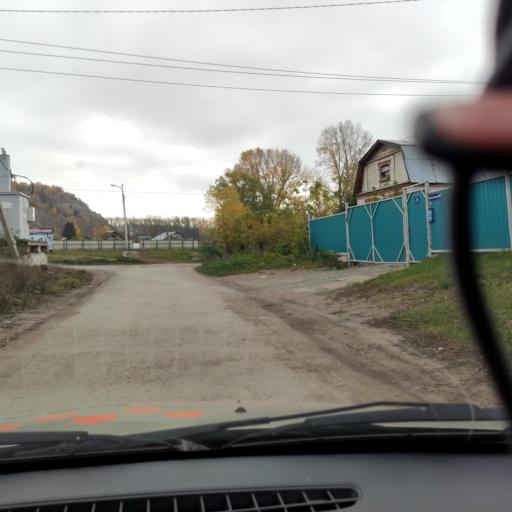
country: RU
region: Bashkortostan
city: Ufa
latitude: 54.7284
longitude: 55.9072
